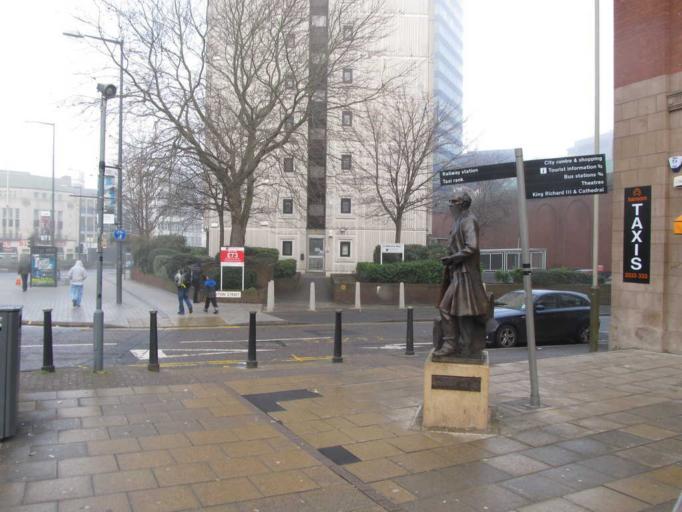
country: GB
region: England
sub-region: City of Leicester
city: Leicester
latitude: 52.6314
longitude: -1.1257
